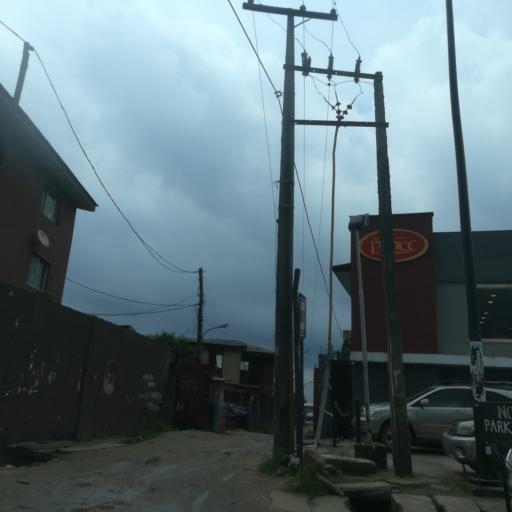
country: NG
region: Lagos
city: Agege
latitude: 6.6025
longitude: 3.3072
